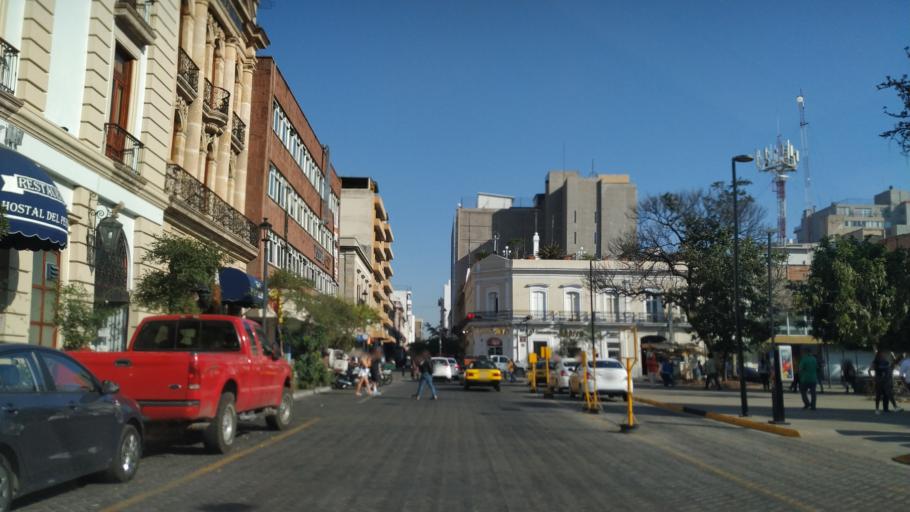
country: MX
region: Jalisco
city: Guadalajara
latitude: 20.6722
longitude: -103.3479
